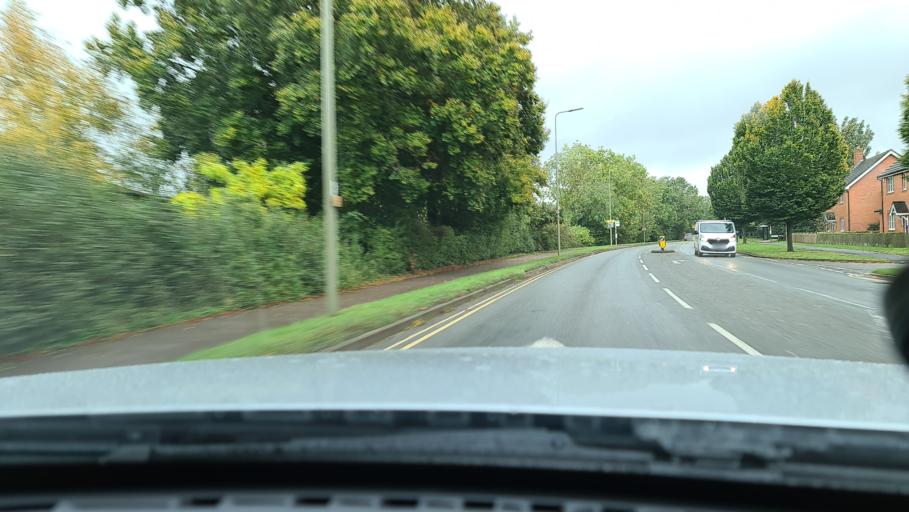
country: GB
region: England
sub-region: Oxfordshire
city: Banbury
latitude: 52.0481
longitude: -1.3325
